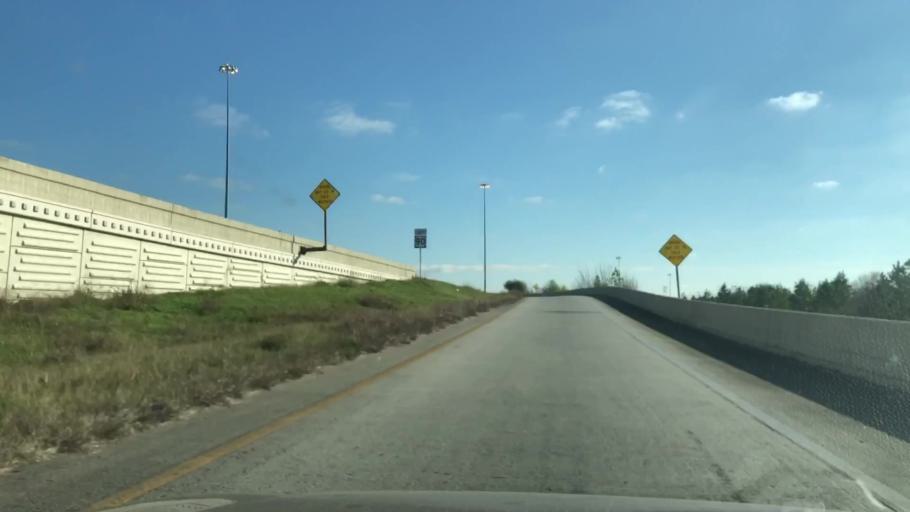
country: US
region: Texas
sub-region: Harris County
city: Jacinto City
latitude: 29.7738
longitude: -95.2609
